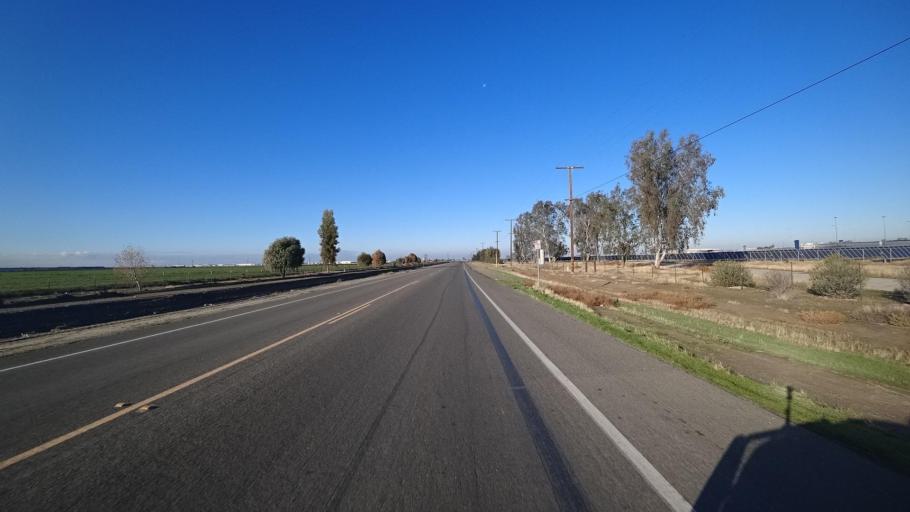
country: US
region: California
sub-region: Kern County
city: Delano
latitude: 35.7759
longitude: -119.3064
